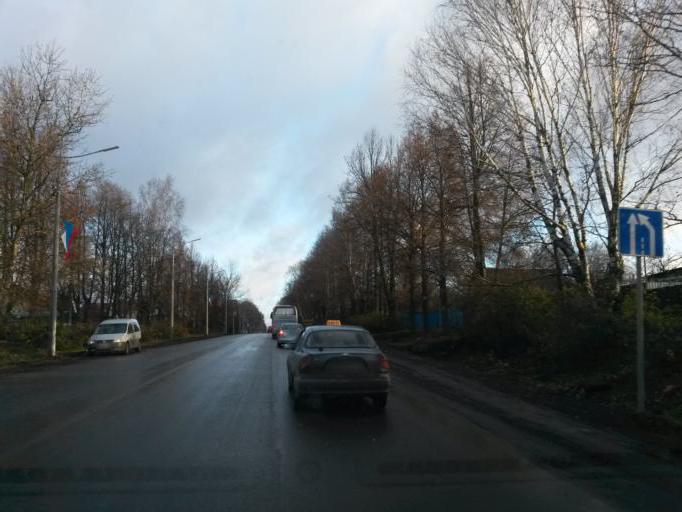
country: RU
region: Jaroslavl
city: Pereslavl'-Zalesskiy
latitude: 56.7476
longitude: 38.8593
